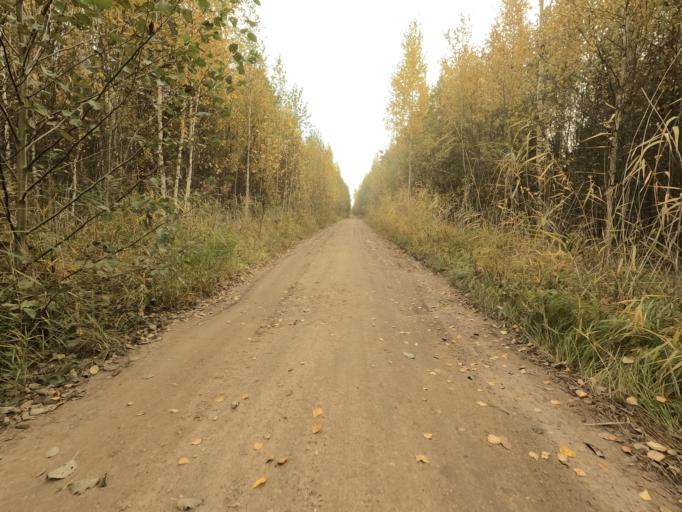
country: RU
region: Novgorod
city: Pankovka
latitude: 58.8771
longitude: 30.8660
